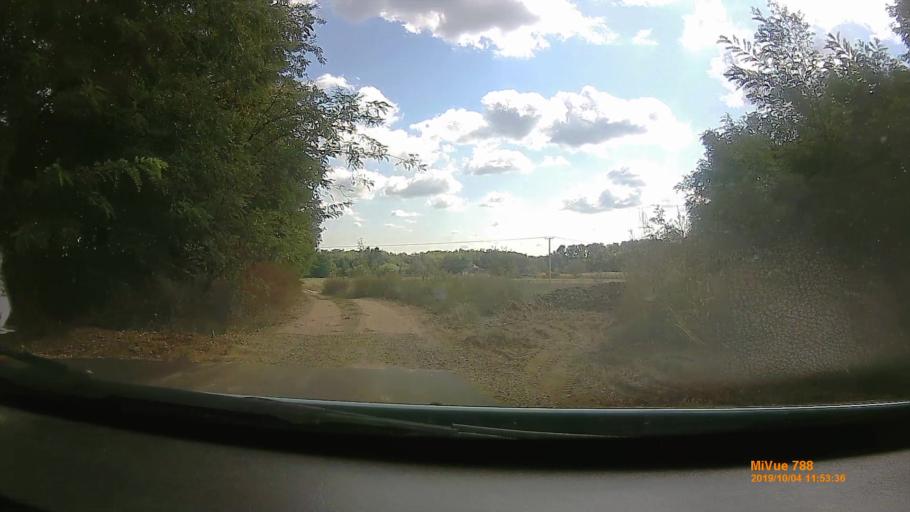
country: HU
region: Szabolcs-Szatmar-Bereg
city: Nyirtelek
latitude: 48.0096
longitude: 21.6765
